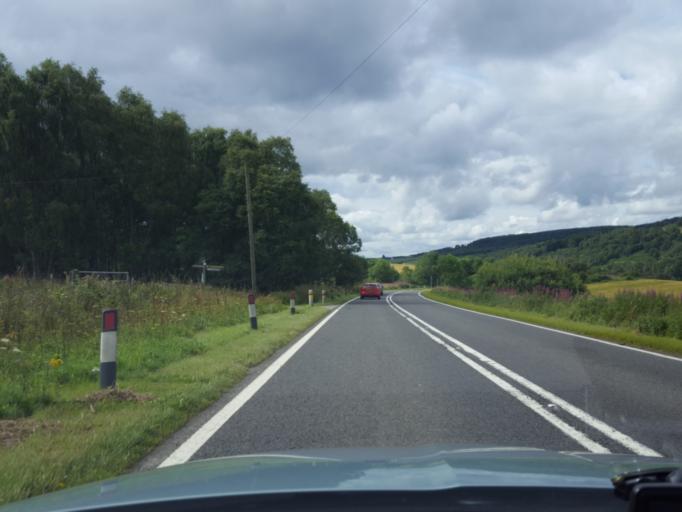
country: GB
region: Scotland
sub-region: Moray
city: Rothes
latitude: 57.4456
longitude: -3.2710
